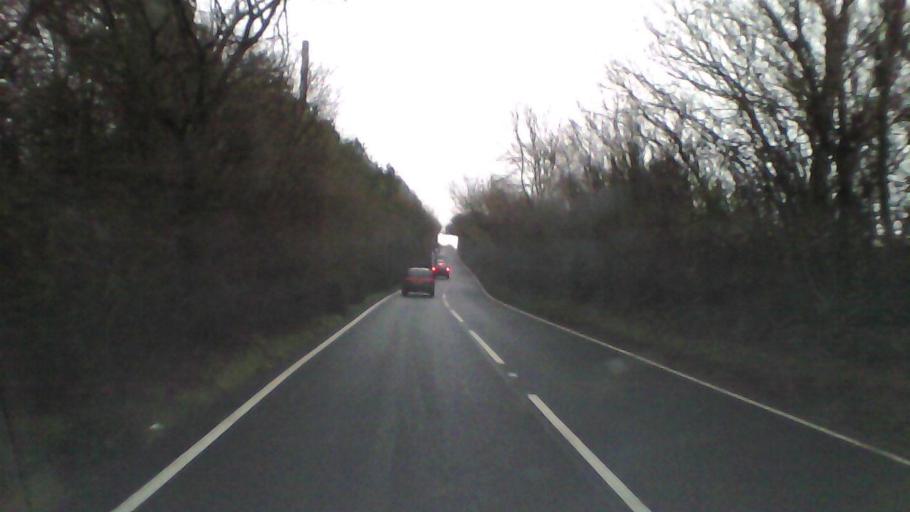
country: GB
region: England
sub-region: Isle of Wight
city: Newport
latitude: 50.6914
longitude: -1.2528
